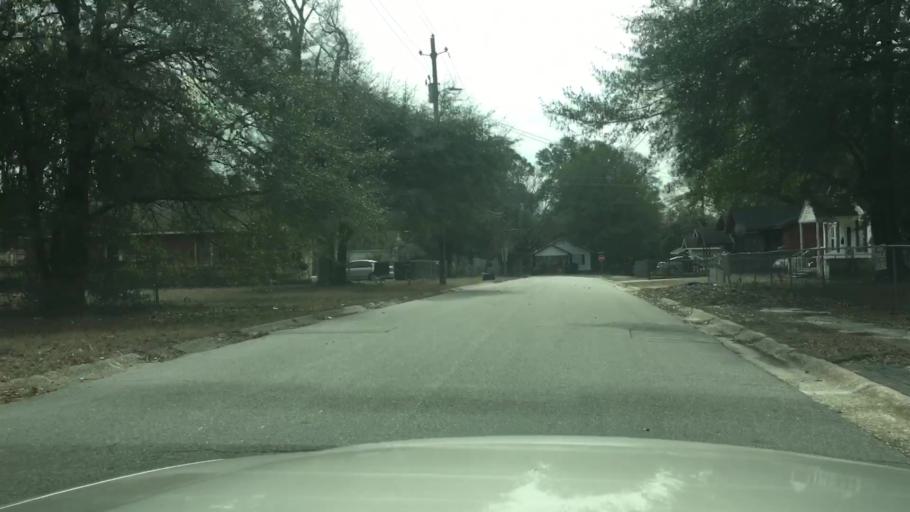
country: US
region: North Carolina
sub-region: Cumberland County
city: Fayetteville
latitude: 35.0538
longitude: -78.8993
